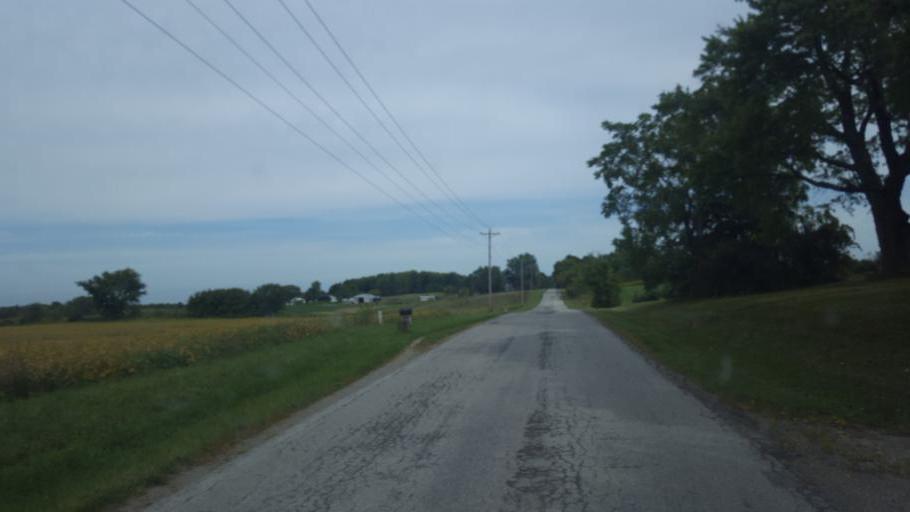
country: US
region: Ohio
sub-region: Knox County
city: Centerburg
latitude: 40.3583
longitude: -82.7251
